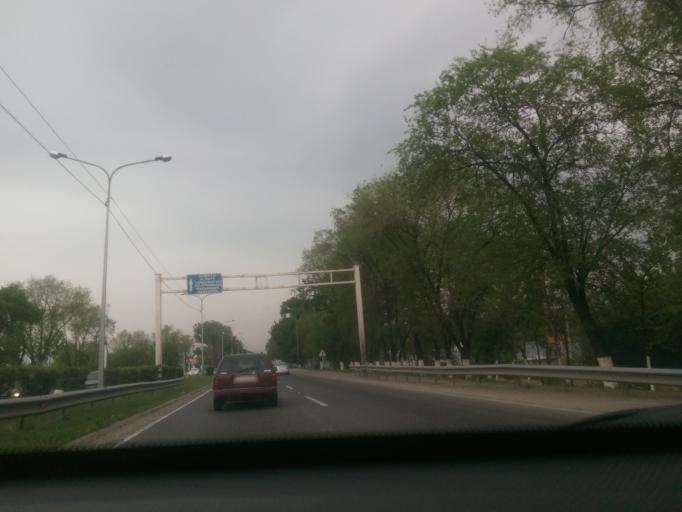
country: KZ
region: Almaty Oblysy
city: Burunday
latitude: 43.2260
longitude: 76.7353
